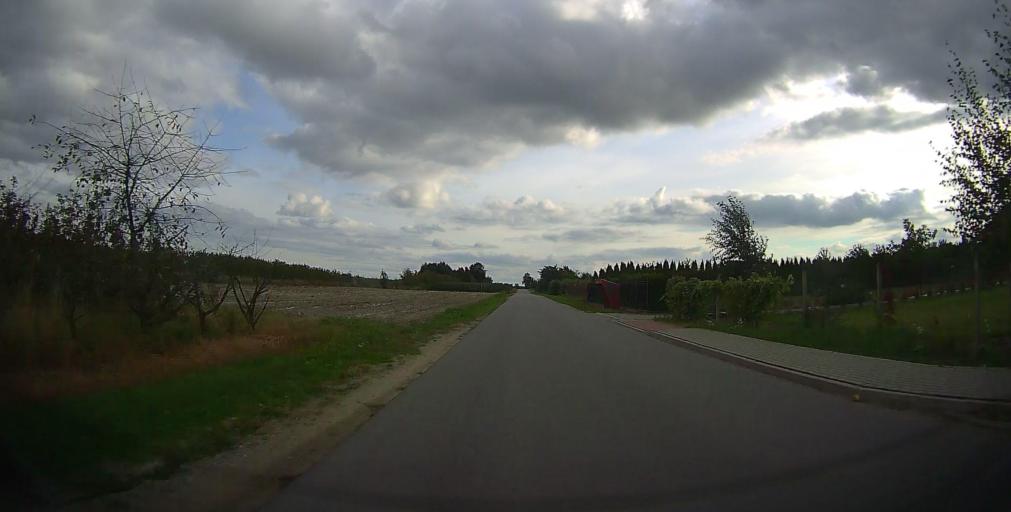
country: PL
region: Masovian Voivodeship
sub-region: Powiat bialobrzeski
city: Promna
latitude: 51.7212
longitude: 20.9586
